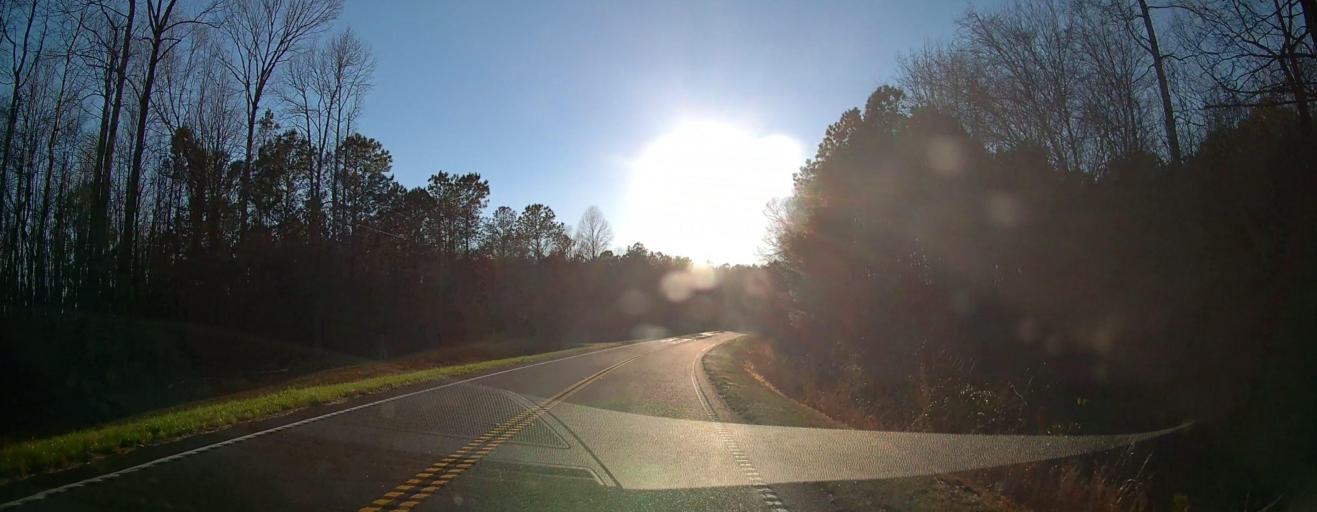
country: US
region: Georgia
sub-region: Talbot County
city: Talbotton
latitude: 32.6584
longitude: -84.6446
